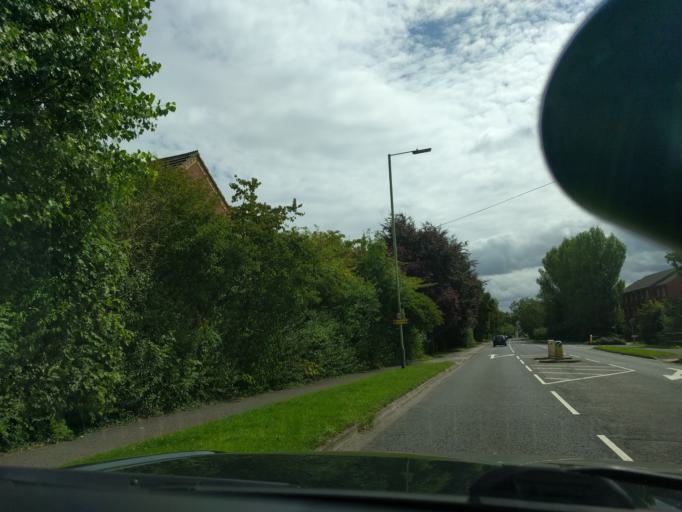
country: GB
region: England
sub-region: Wiltshire
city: Chippenham
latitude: 51.4679
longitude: -2.1397
